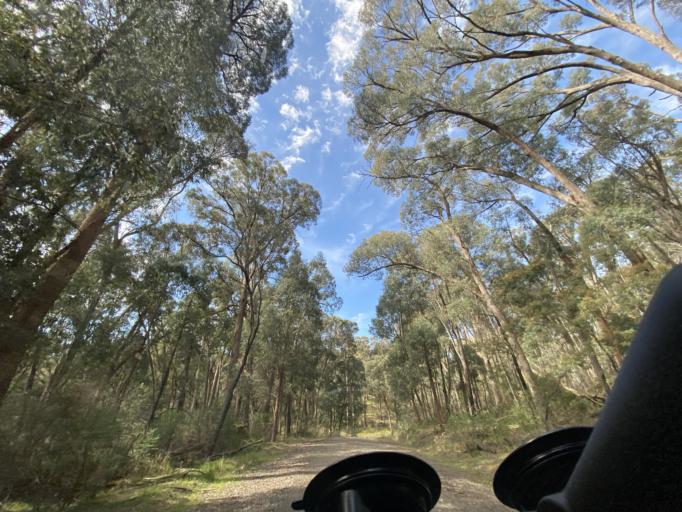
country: AU
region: Victoria
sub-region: Mansfield
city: Mansfield
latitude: -36.8133
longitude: 146.1032
